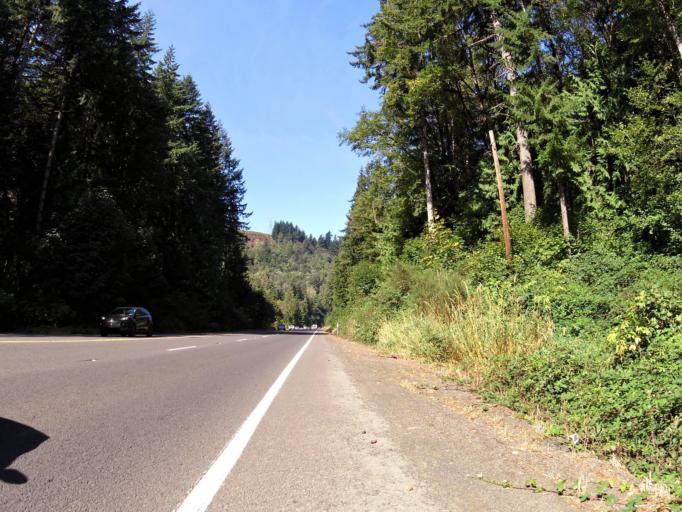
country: US
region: Washington
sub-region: Wahkiakum County
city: Cathlamet
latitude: 46.1565
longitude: -123.4229
